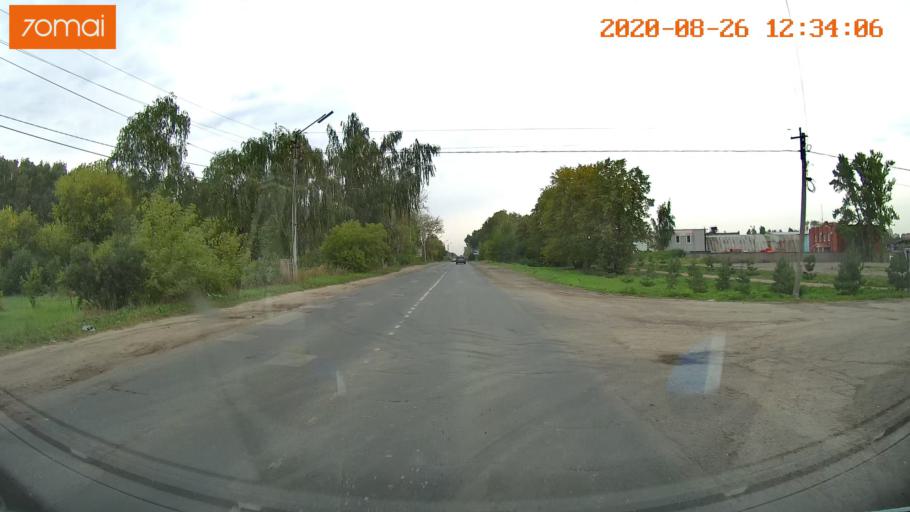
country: RU
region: Rjazan
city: Ryazan'
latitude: 54.5857
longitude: 39.7724
